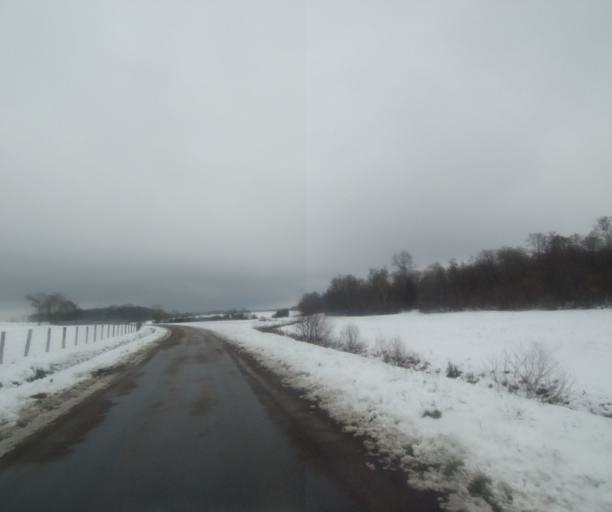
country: FR
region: Champagne-Ardenne
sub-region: Departement de la Haute-Marne
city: Laneuville-a-Remy
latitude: 48.4622
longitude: 4.8306
